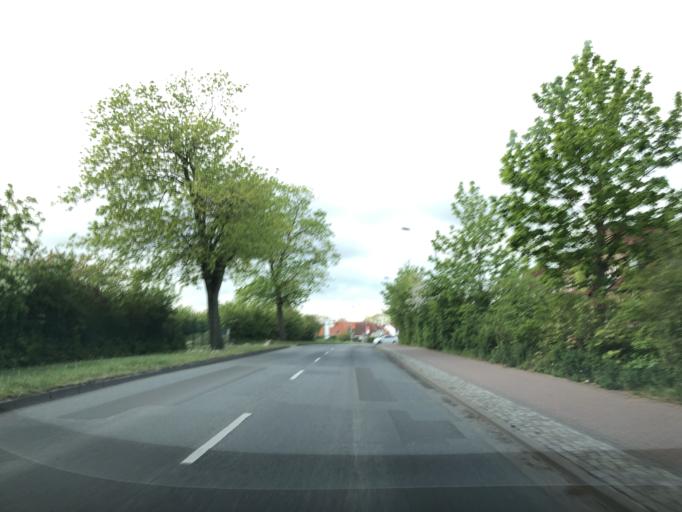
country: DE
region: Mecklenburg-Vorpommern
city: Guestrow
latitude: 53.7760
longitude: 12.1718
